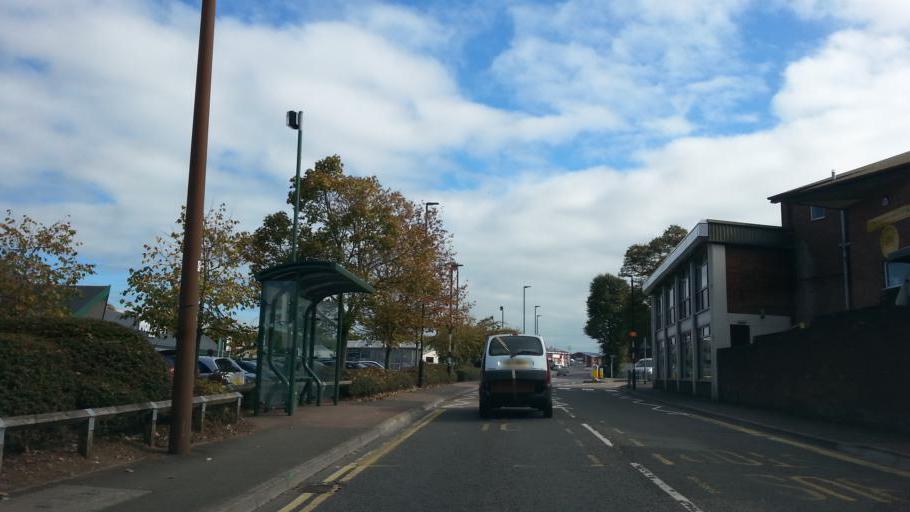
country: GB
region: England
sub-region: Herefordshire
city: Ross on Wye
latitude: 51.9156
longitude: -2.5796
